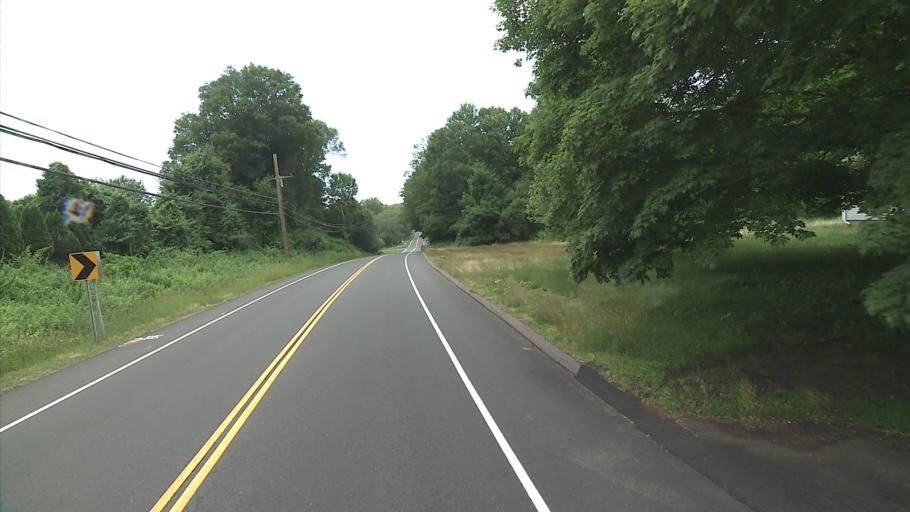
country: US
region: Connecticut
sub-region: Hartford County
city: Manchester
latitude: 41.7092
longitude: -72.5039
